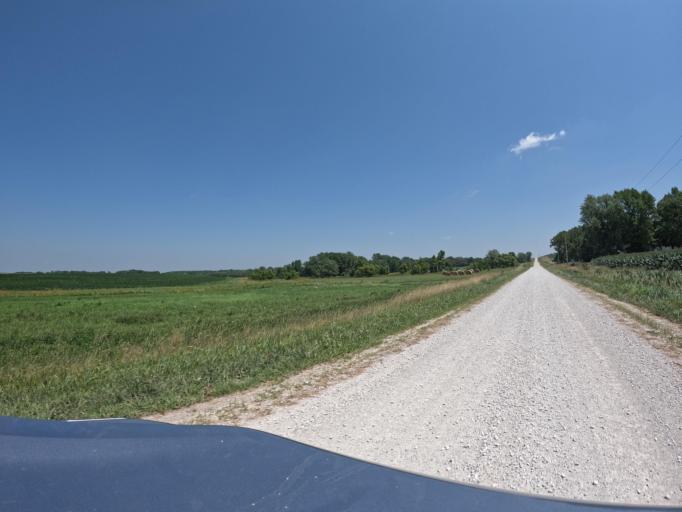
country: US
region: Iowa
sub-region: Keokuk County
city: Sigourney
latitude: 41.2868
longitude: -92.1731
